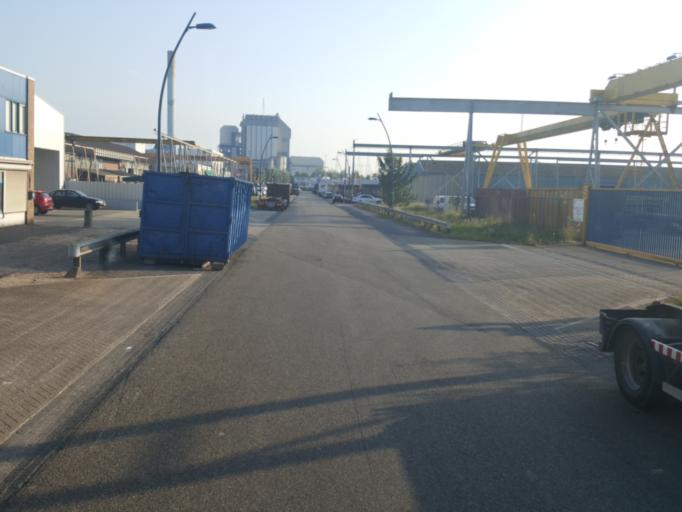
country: NL
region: Gelderland
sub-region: Gemeente Nijmegen
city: Nijmegen
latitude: 51.8486
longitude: 5.8249
